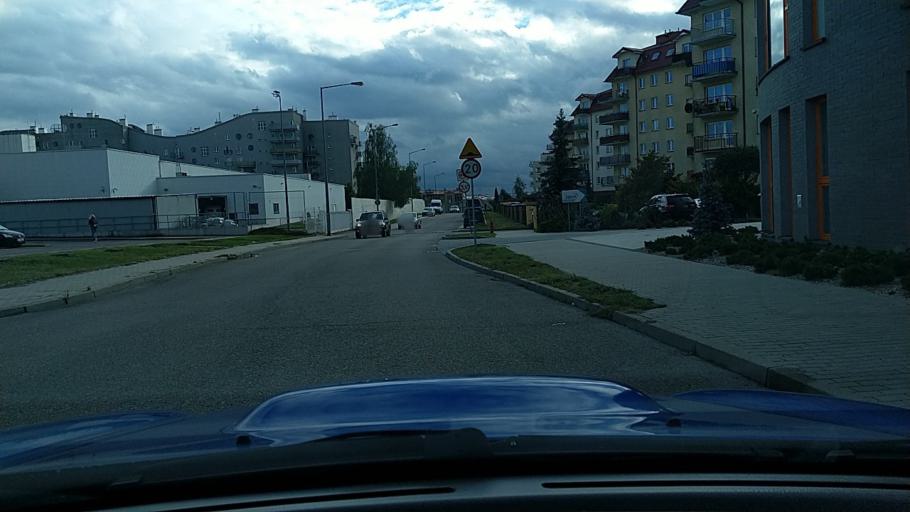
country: PL
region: Warmian-Masurian Voivodeship
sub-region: Powiat olsztynski
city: Olsztyn
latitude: 53.7648
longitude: 20.4901
